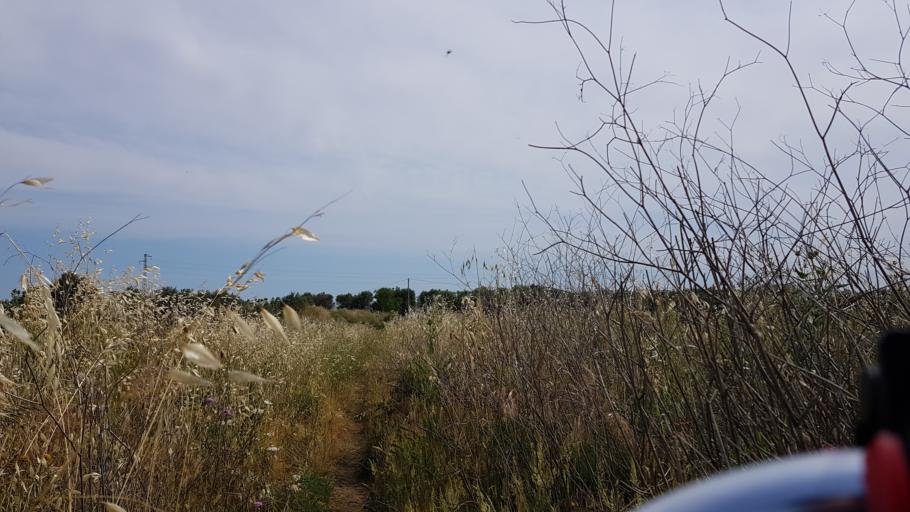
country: IT
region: Apulia
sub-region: Provincia di Brindisi
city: San Vito dei Normanni
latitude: 40.6569
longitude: 17.8027
